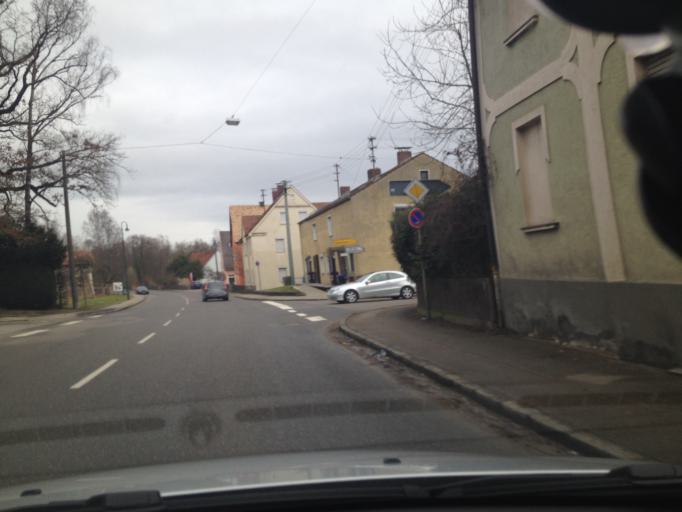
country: DE
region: Bavaria
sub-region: Swabia
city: Aystetten
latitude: 48.4055
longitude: 10.8094
